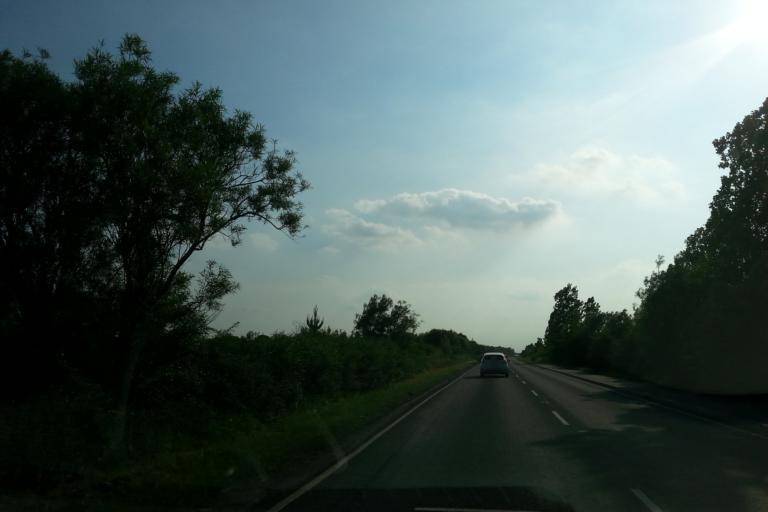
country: GB
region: England
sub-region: Cambridgeshire
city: Needingworth
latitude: 52.3408
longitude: -0.0154
